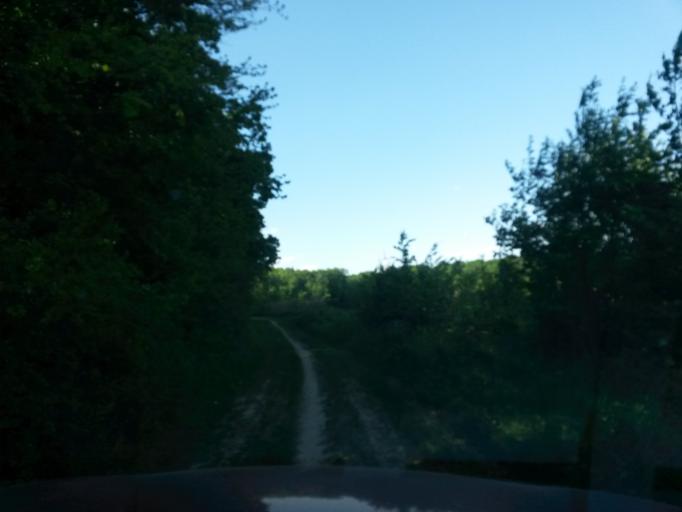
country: SK
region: Kosicky
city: Kosice
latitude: 48.6891
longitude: 21.1820
